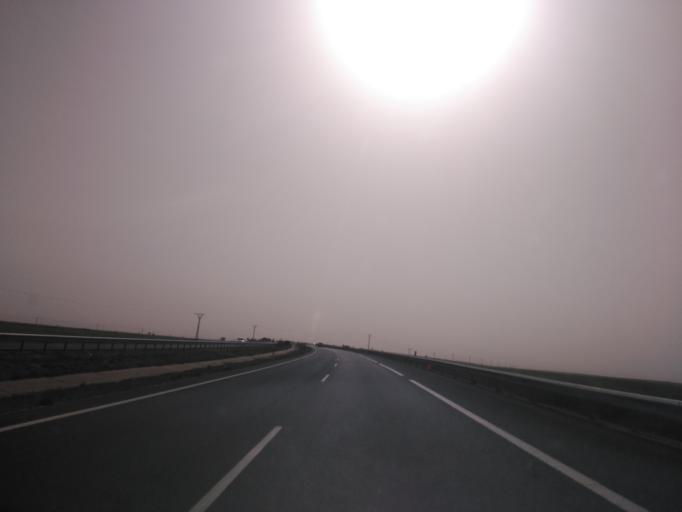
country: ES
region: Castille and Leon
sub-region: Provincia de Palencia
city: Marcilla de Campos
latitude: 42.3137
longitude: -4.4023
